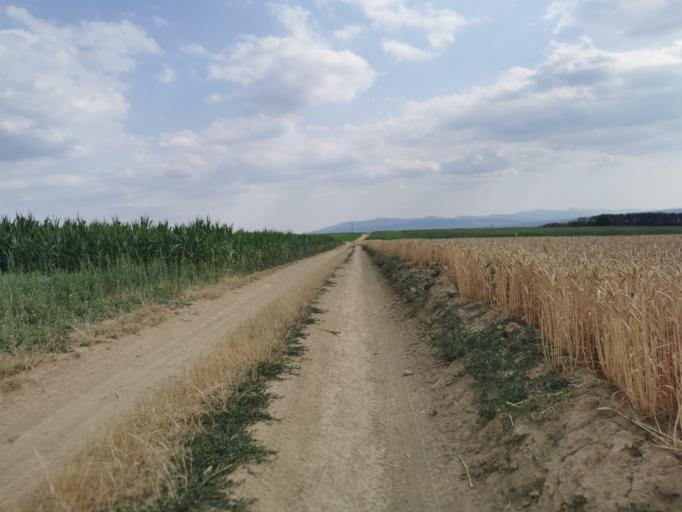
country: SK
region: Trnavsky
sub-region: Okres Senica
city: Senica
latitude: 48.6949
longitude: 17.4213
